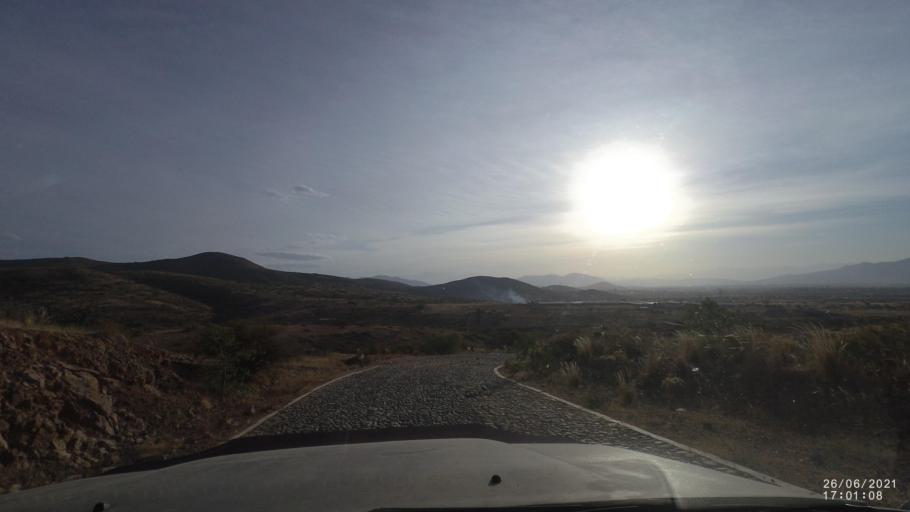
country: BO
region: Cochabamba
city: Cliza
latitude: -17.6638
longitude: -65.9104
